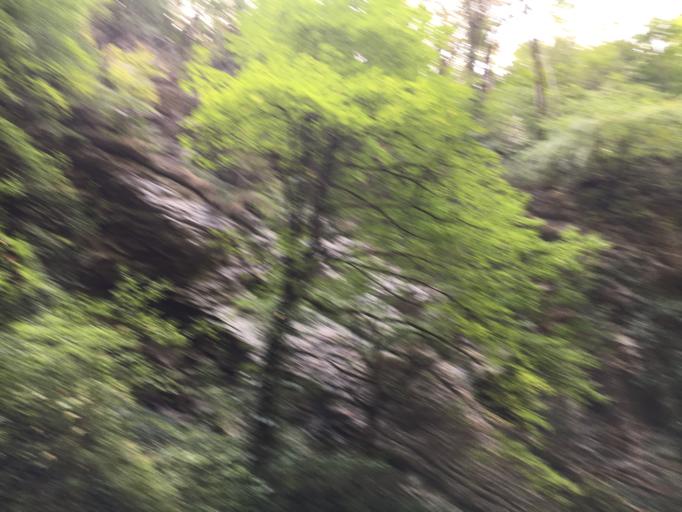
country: RU
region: Krasnodarskiy
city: Tuapse
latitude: 44.2625
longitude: 39.2017
